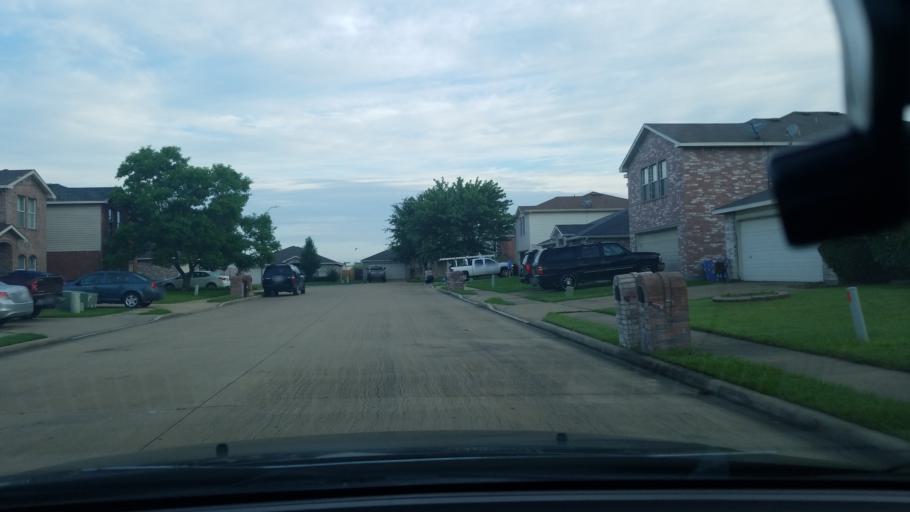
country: US
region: Texas
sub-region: Dallas County
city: Balch Springs
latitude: 32.7647
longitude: -96.6451
